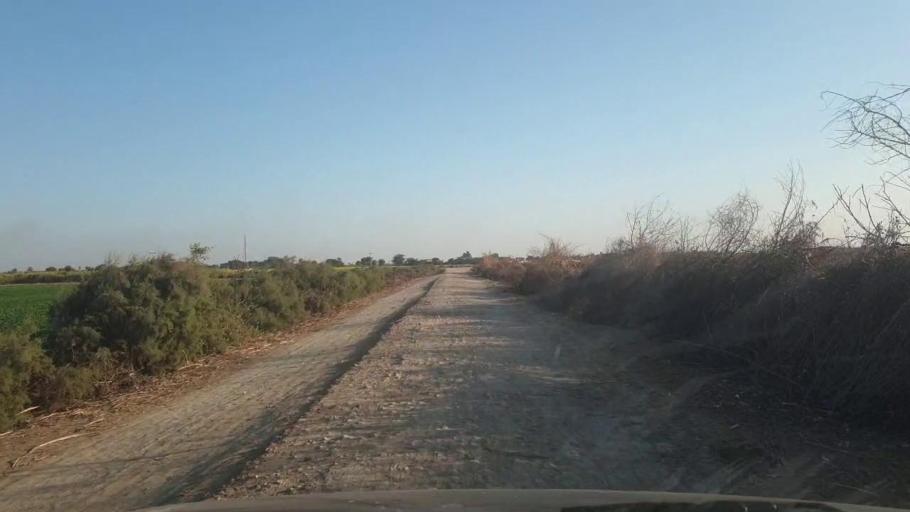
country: PK
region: Sindh
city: Sinjhoro
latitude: 26.0403
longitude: 68.8702
